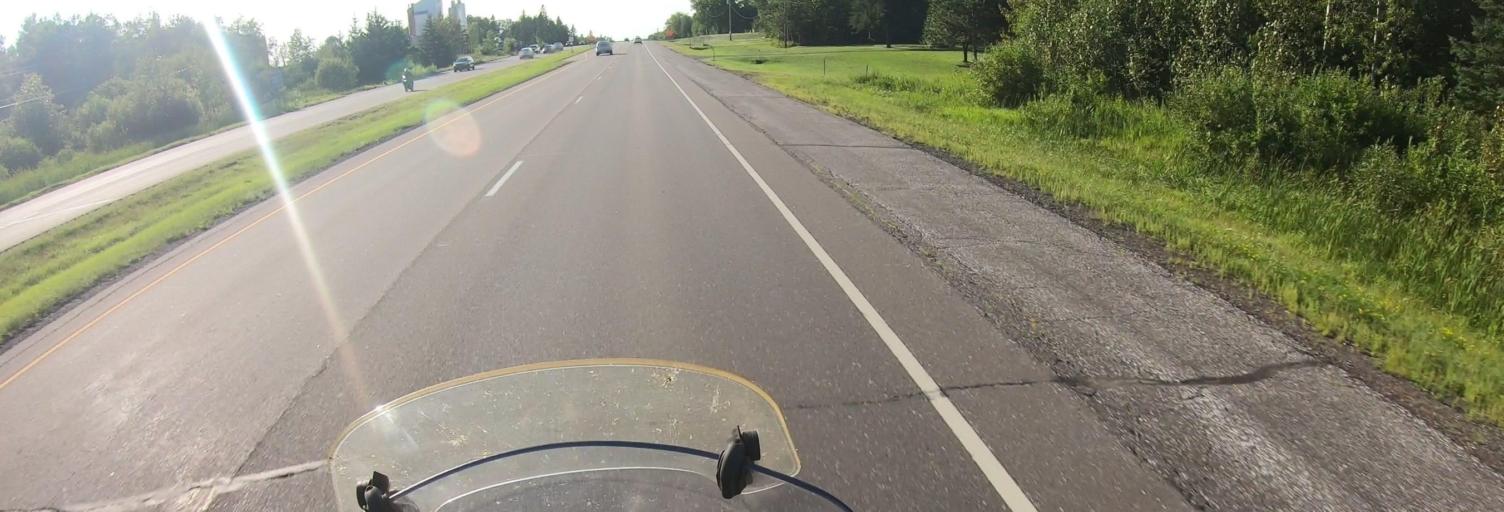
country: US
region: Minnesota
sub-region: Saint Louis County
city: Hermantown
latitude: 46.8458
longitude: -92.2626
